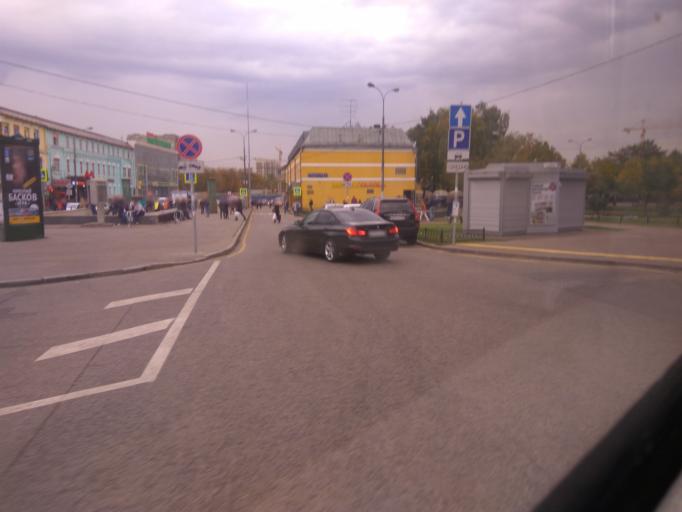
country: RU
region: Moscow
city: Taganskiy
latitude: 55.7469
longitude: 37.6807
